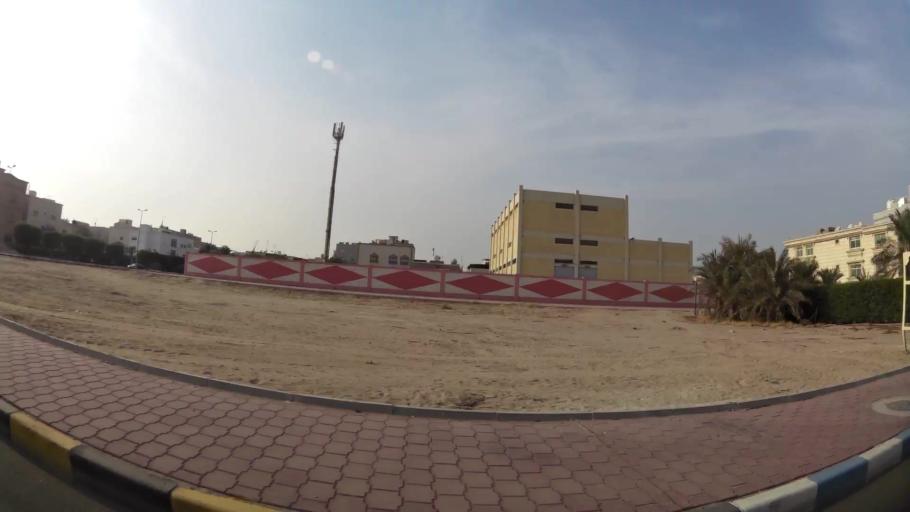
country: KW
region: Mubarak al Kabir
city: Sabah as Salim
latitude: 29.2514
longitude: 48.0545
